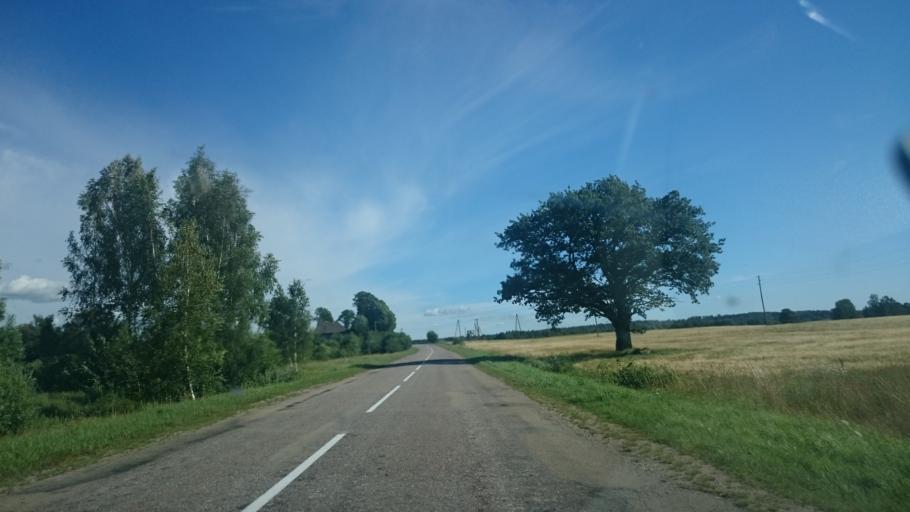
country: LV
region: Aizpute
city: Aizpute
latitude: 56.7180
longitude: 21.7593
